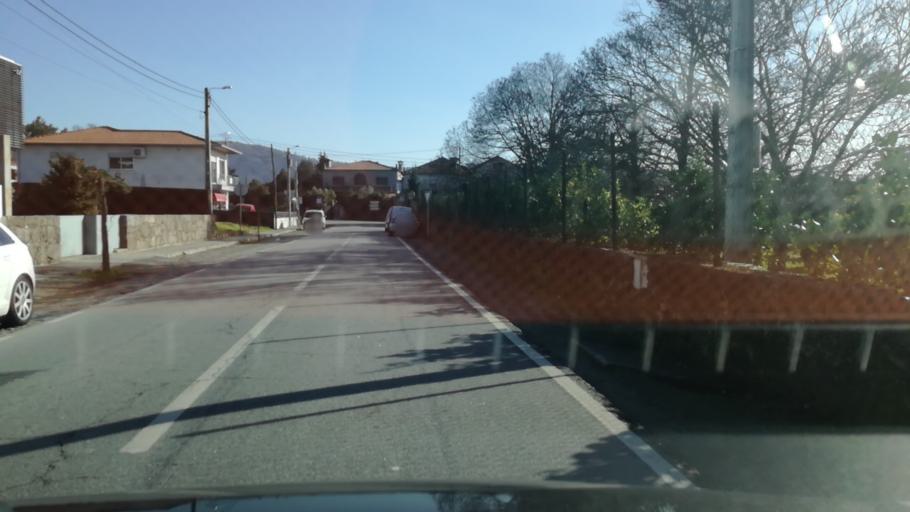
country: PT
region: Braga
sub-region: Guimaraes
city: Ponte
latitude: 41.5155
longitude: -8.3131
